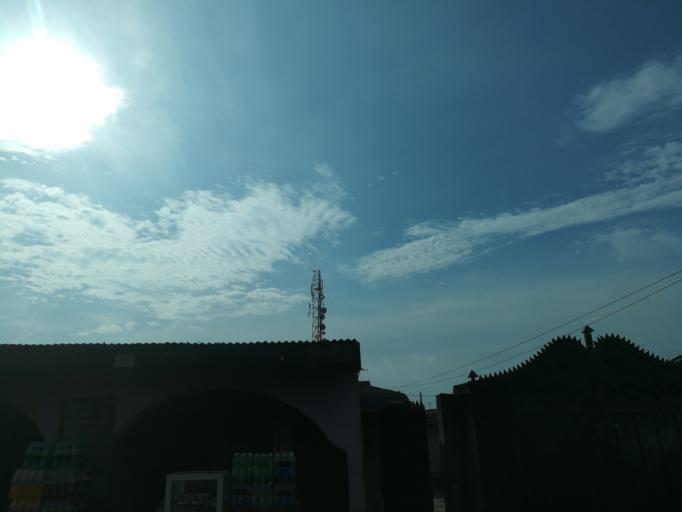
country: NG
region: Lagos
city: Ojota
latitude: 6.6051
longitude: 3.4212
